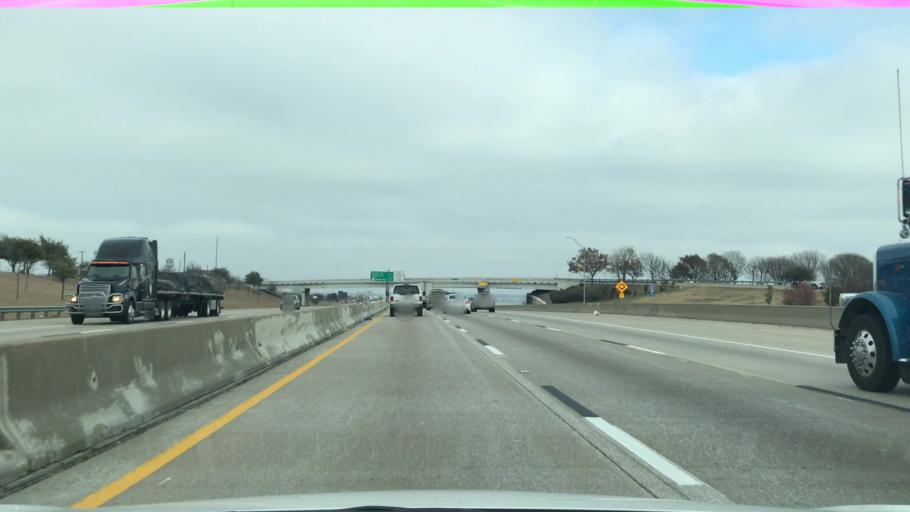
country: US
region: Texas
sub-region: Dallas County
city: Rowlett
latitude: 32.8752
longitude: -96.5207
